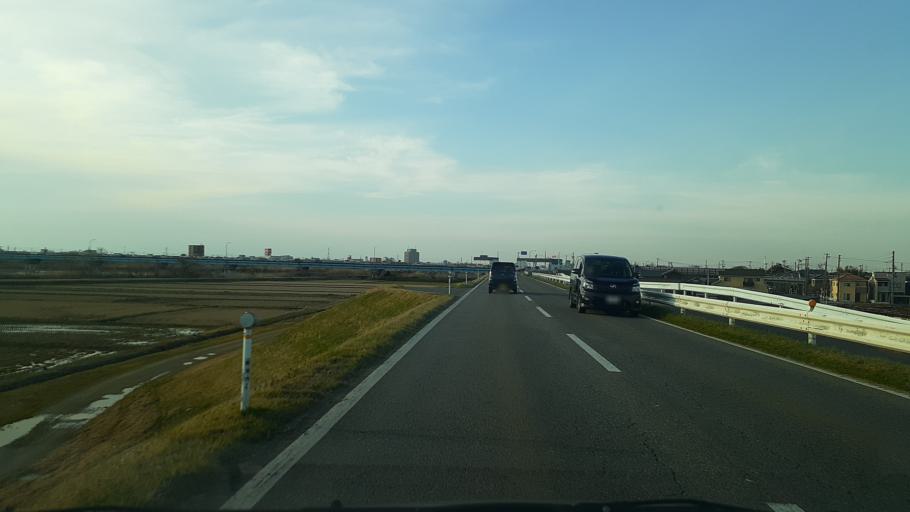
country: JP
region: Niigata
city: Niigata-shi
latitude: 37.8519
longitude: 139.0260
